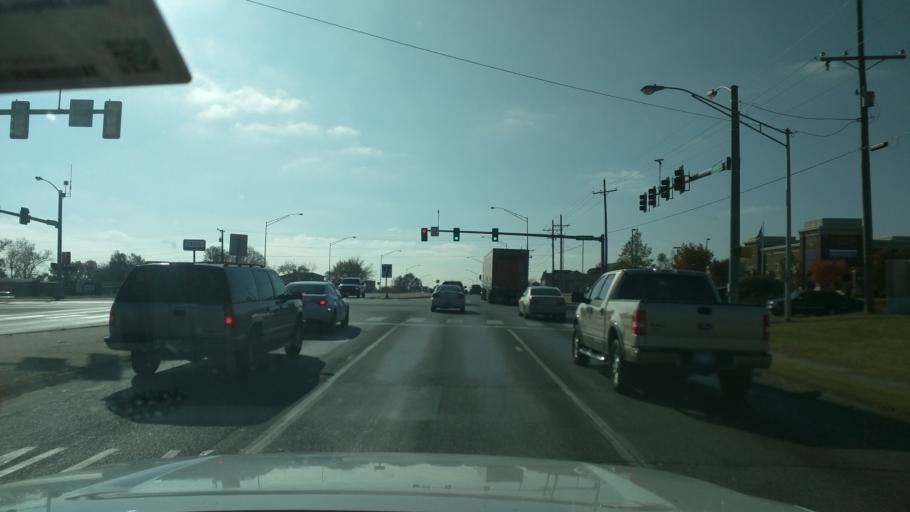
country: US
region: Oklahoma
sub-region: Washington County
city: Bartlesville
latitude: 36.7285
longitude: -95.9352
